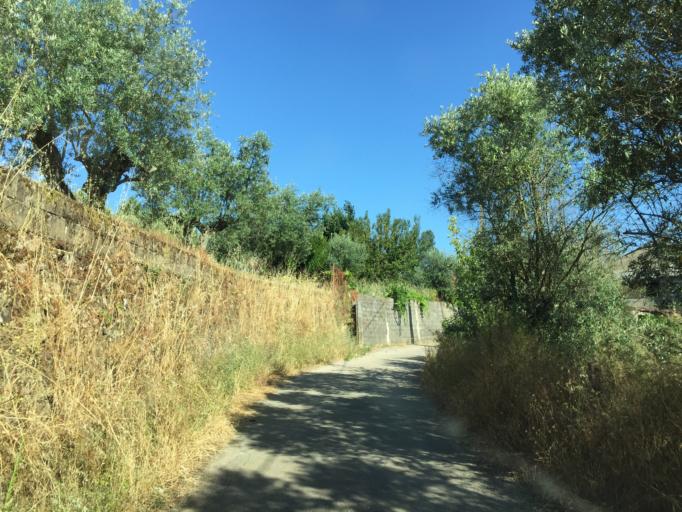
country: PT
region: Santarem
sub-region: Ferreira do Zezere
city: Ferreira do Zezere
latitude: 39.6014
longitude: -8.2983
